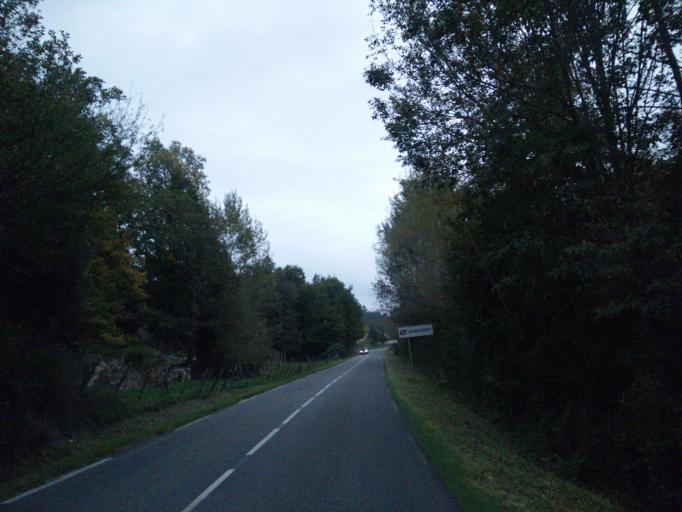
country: FR
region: Aquitaine
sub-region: Departement de la Dordogne
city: Carsac-Aillac
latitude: 44.7959
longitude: 1.3038
